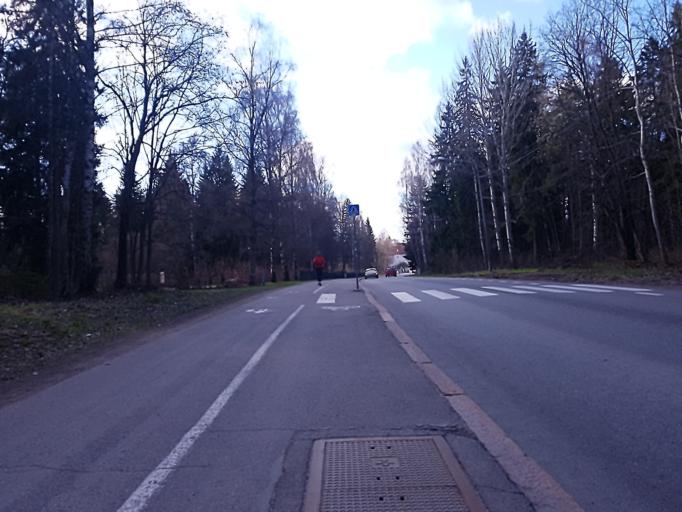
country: FI
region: Uusimaa
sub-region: Helsinki
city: Helsinki
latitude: 60.2109
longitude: 24.9614
